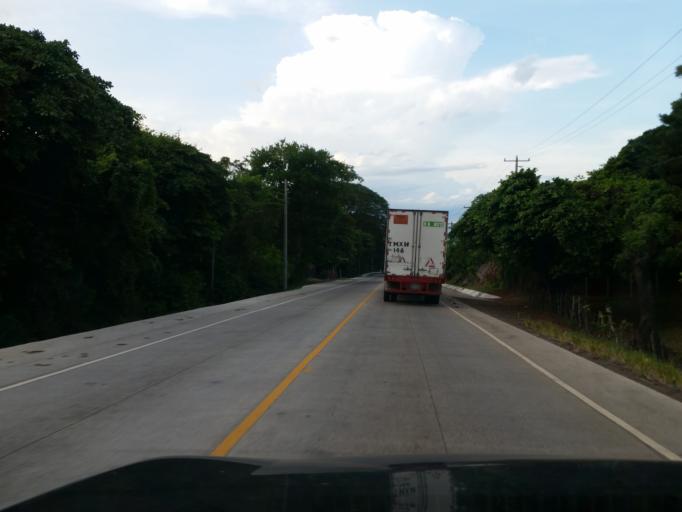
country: NI
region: Managua
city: Ciudad Sandino
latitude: 12.0824
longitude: -86.3606
